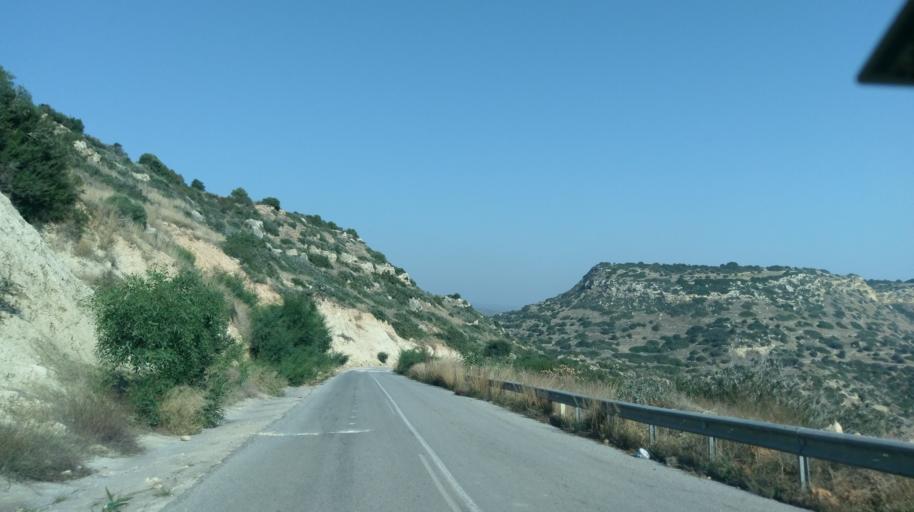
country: CY
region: Ammochostos
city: Leonarisso
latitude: 35.4924
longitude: 34.2239
